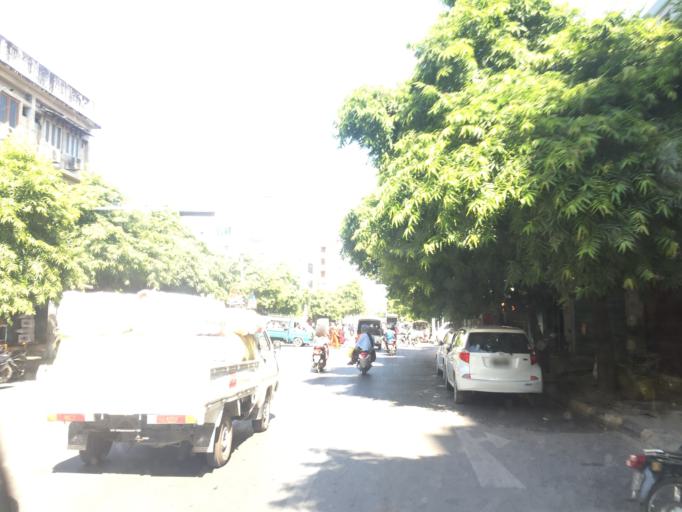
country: MM
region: Mandalay
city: Mandalay
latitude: 21.9834
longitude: 96.0800
